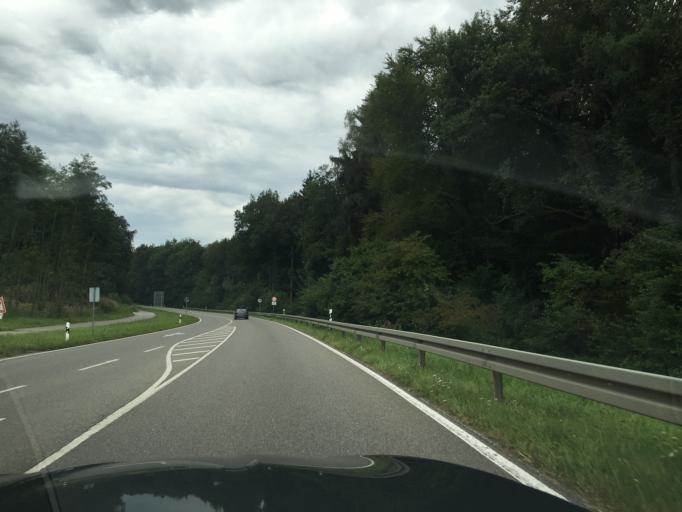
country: DE
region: Baden-Wuerttemberg
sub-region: Freiburg Region
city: Stockach
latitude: 47.8363
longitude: 8.9890
